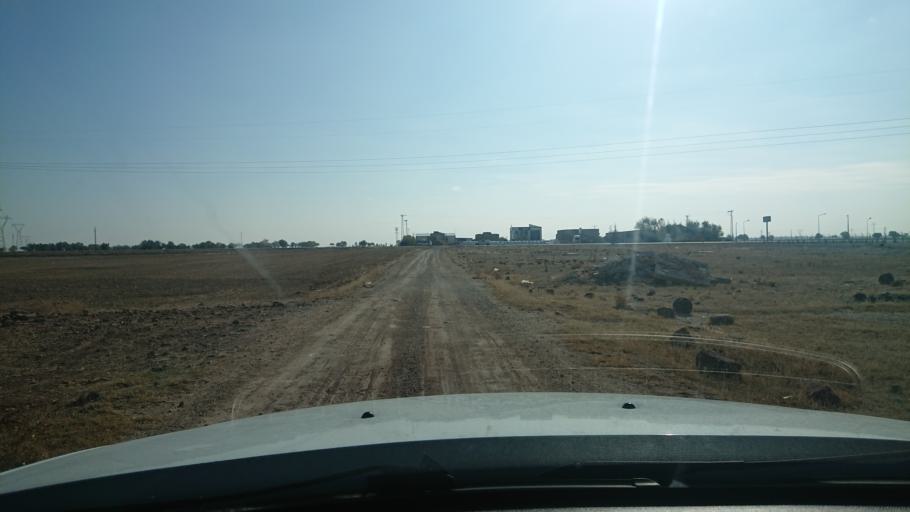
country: TR
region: Aksaray
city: Sultanhani
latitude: 38.2538
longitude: 33.4719
